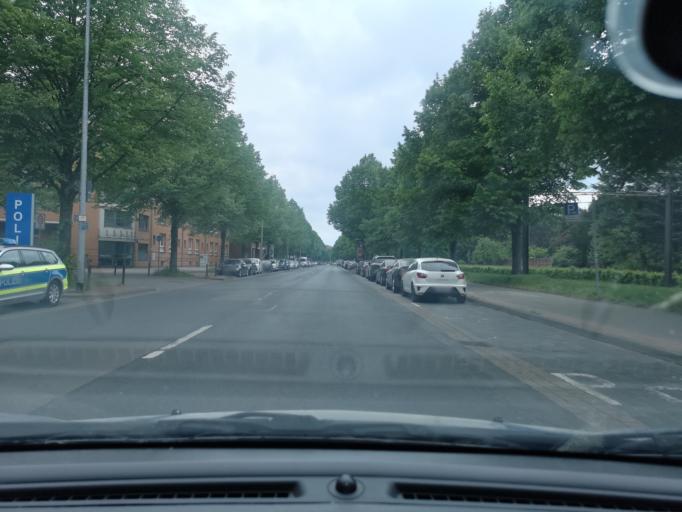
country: DE
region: Lower Saxony
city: Auf der Horst
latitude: 52.4017
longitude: 9.6663
